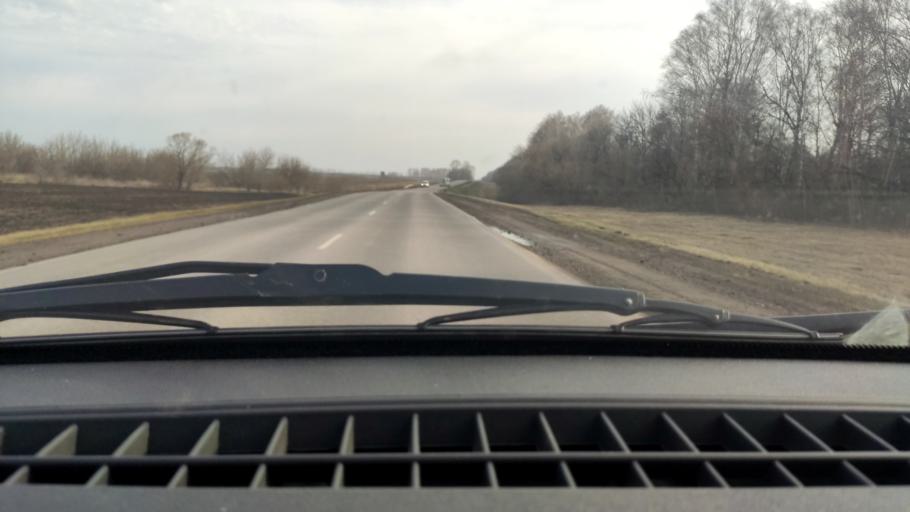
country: RU
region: Bashkortostan
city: Chishmy
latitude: 54.5262
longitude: 55.3017
